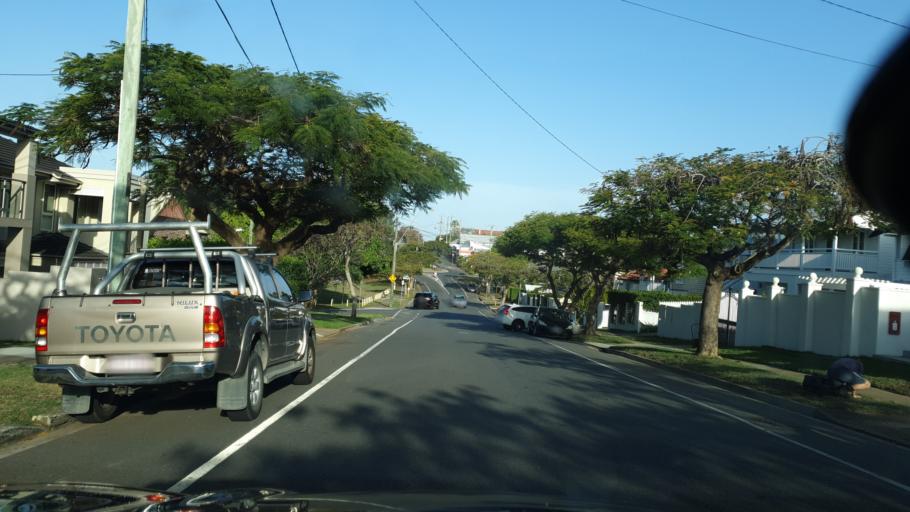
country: AU
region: Queensland
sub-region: Brisbane
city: Ascot
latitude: -27.4300
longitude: 153.0564
